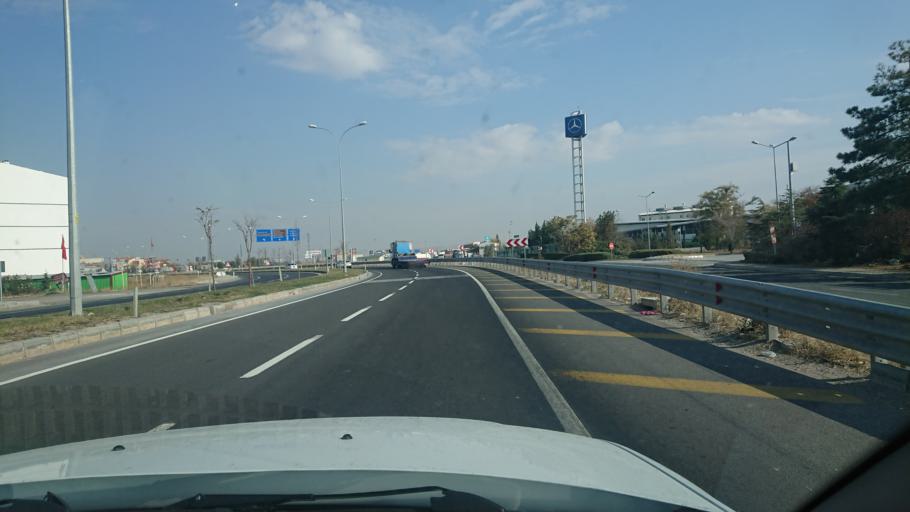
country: TR
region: Aksaray
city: Aksaray
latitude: 38.3532
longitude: 33.9672
